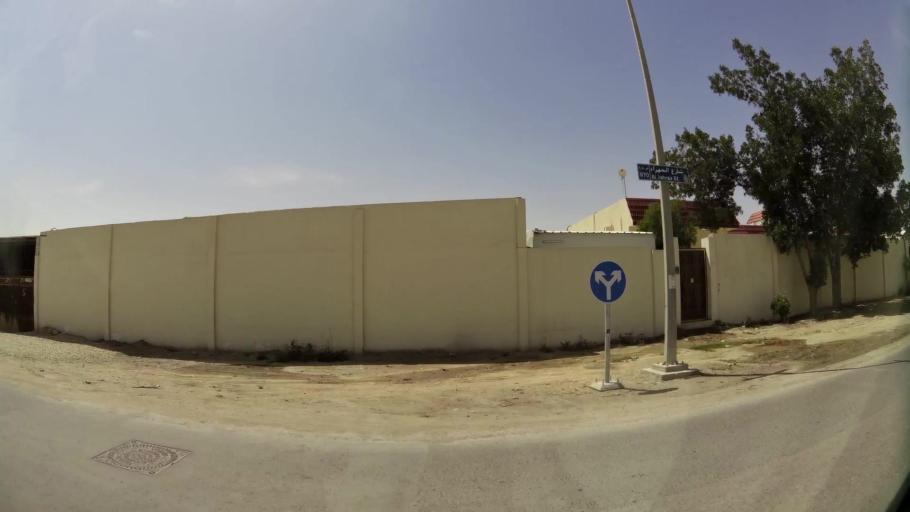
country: QA
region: Baladiyat ar Rayyan
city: Ar Rayyan
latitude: 25.2636
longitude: 51.4110
